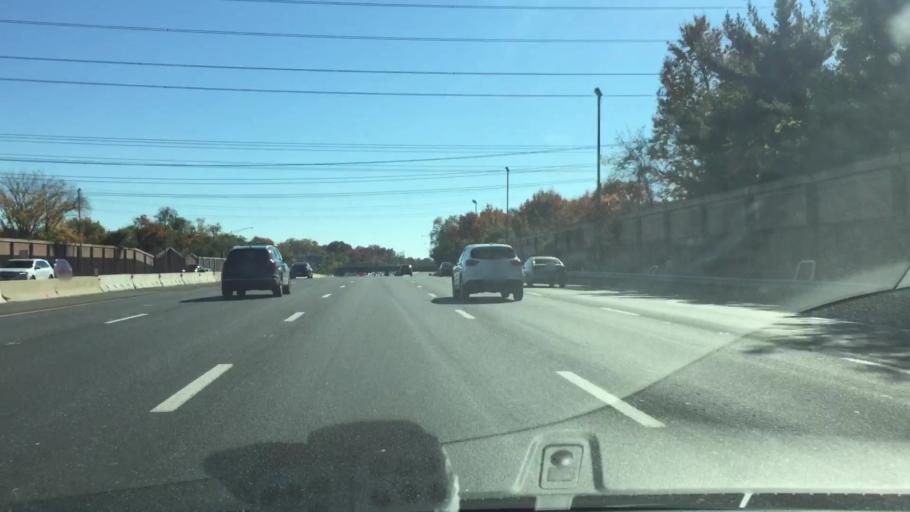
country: US
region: New Jersey
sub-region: Camden County
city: Gloucester City
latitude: 39.8880
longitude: -75.1048
